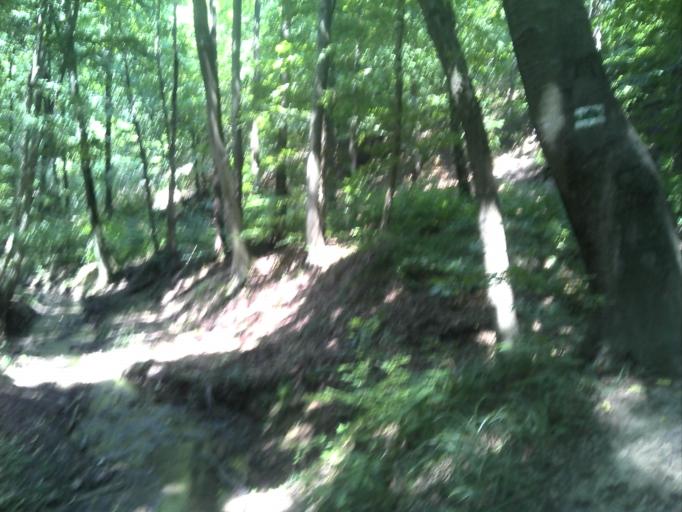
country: HU
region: Baranya
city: Pecs
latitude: 46.1433
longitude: 18.2165
